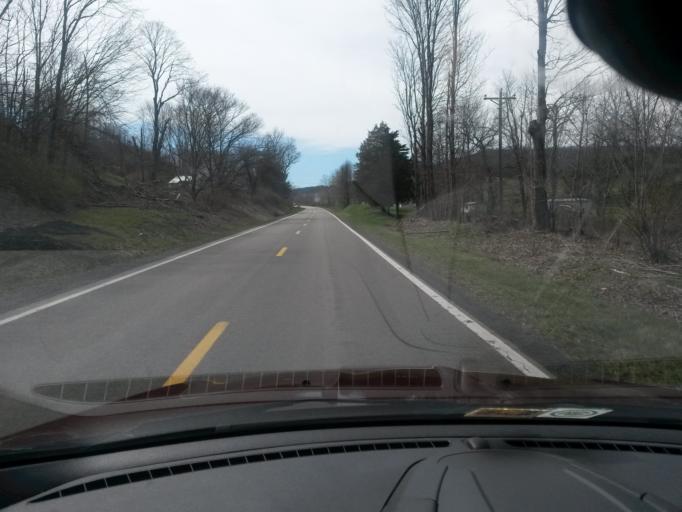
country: US
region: West Virginia
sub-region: Greenbrier County
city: White Sulphur Springs
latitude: 37.6240
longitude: -80.2526
